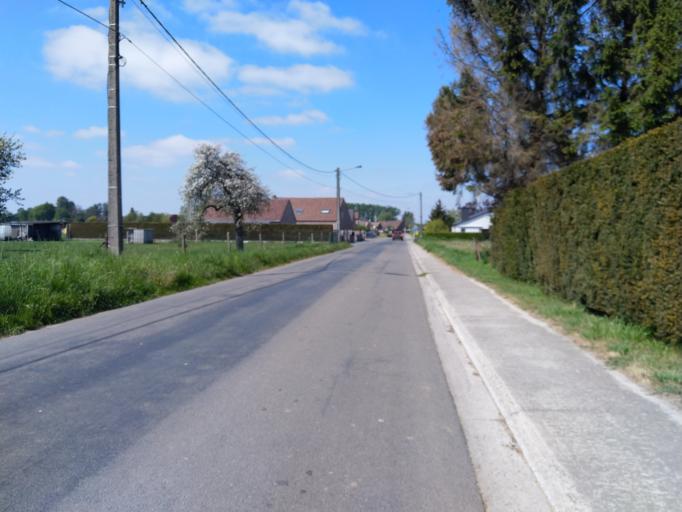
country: BE
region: Wallonia
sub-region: Province du Hainaut
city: Jurbise
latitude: 50.5113
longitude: 3.8752
